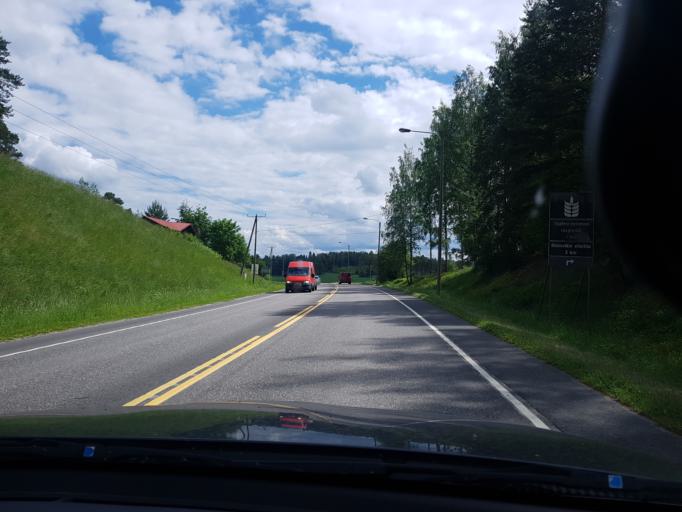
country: FI
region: Pirkanmaa
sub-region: Tampere
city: Paelkaene
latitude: 61.2746
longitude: 24.3464
